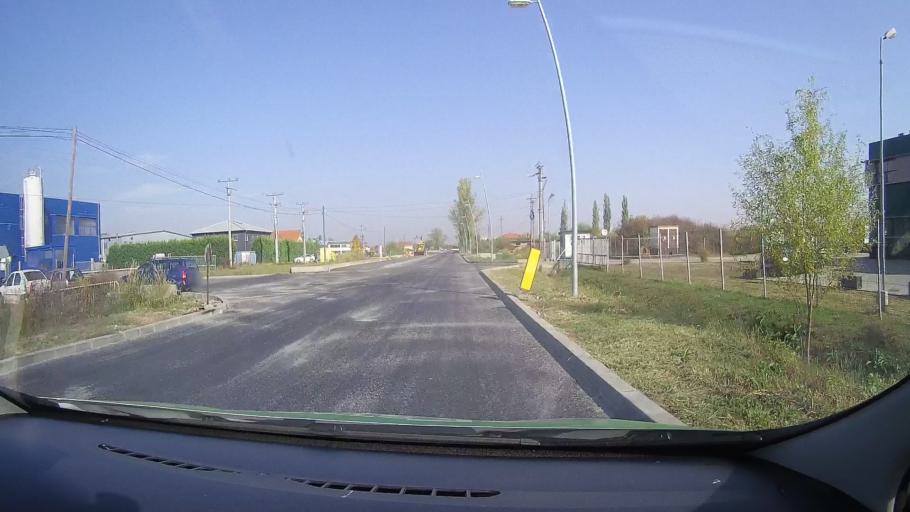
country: RO
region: Bihor
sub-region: Municipiul Salonta
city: Salonta
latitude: 46.7891
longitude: 21.6634
